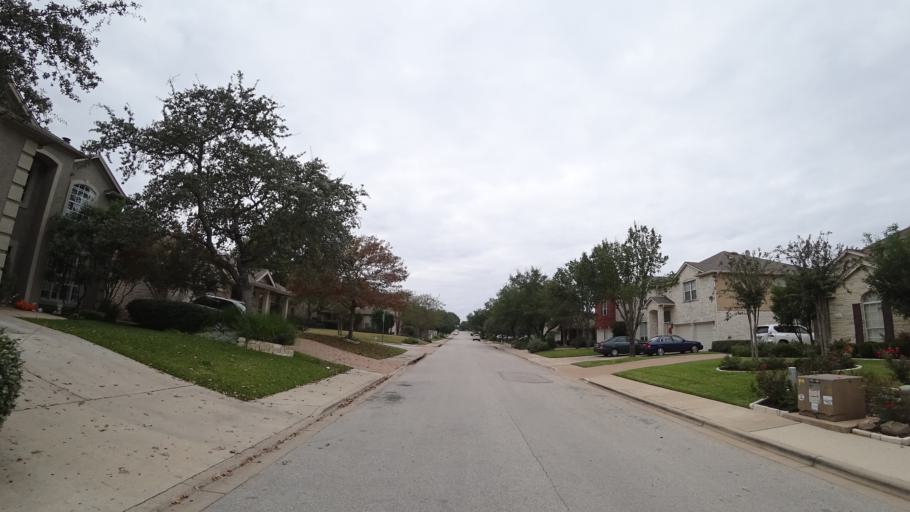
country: US
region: Texas
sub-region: Travis County
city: Bee Cave
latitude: 30.3125
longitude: -97.9150
